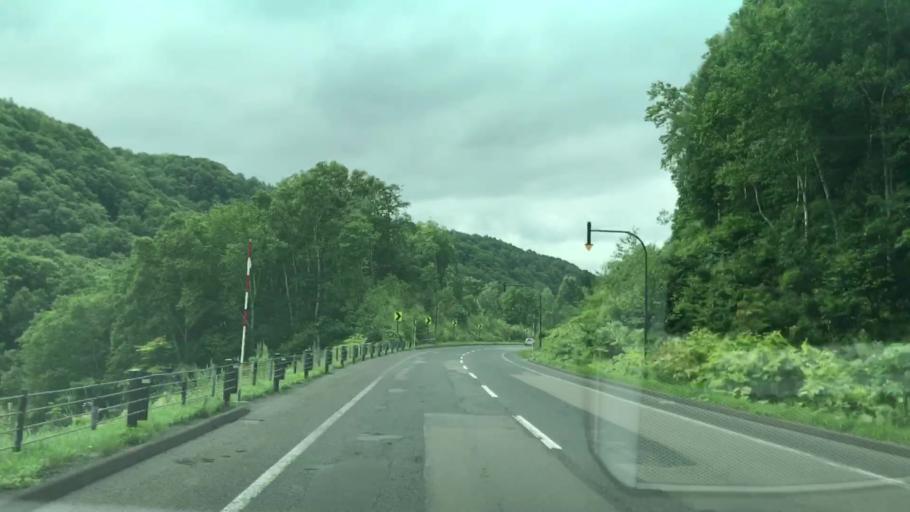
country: JP
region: Hokkaido
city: Yoichi
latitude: 42.9580
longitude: 140.8700
